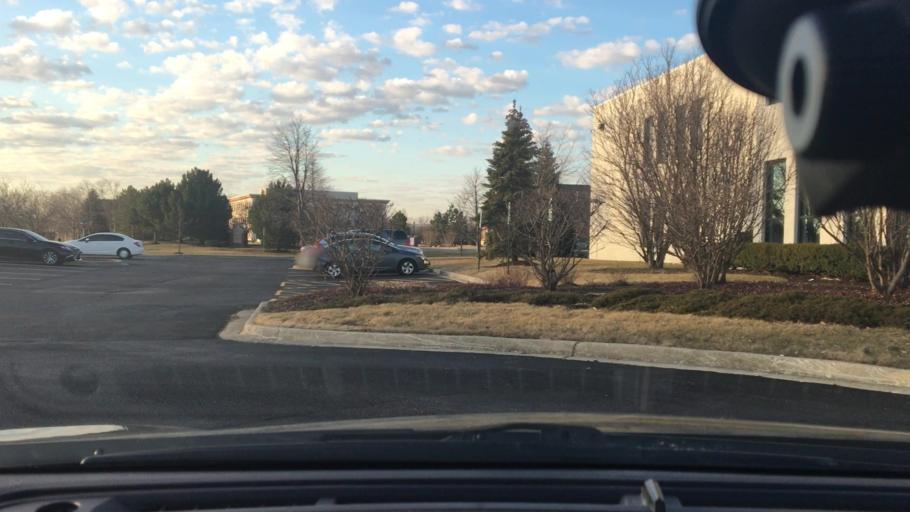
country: US
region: Illinois
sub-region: Cook County
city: Northfield
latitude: 42.1008
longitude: -87.8106
